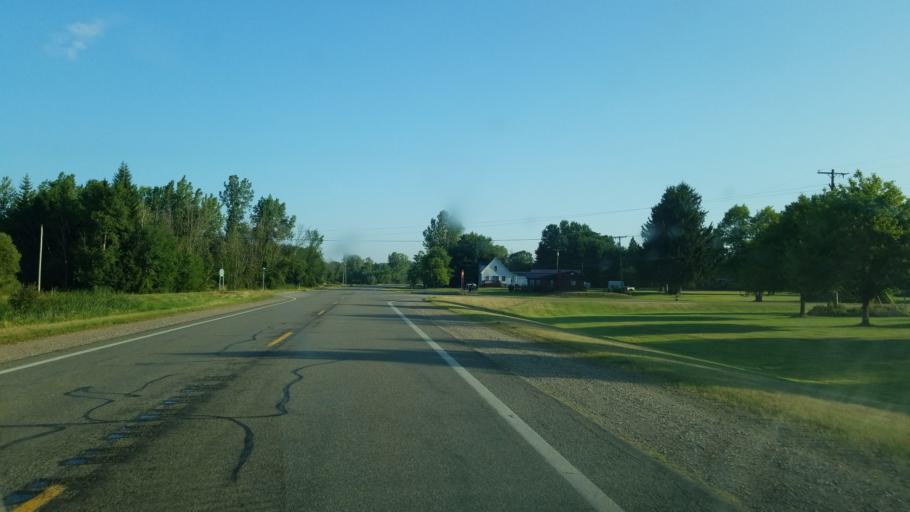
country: US
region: Michigan
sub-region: Montcalm County
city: Stanton
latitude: 43.3281
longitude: -85.0866
